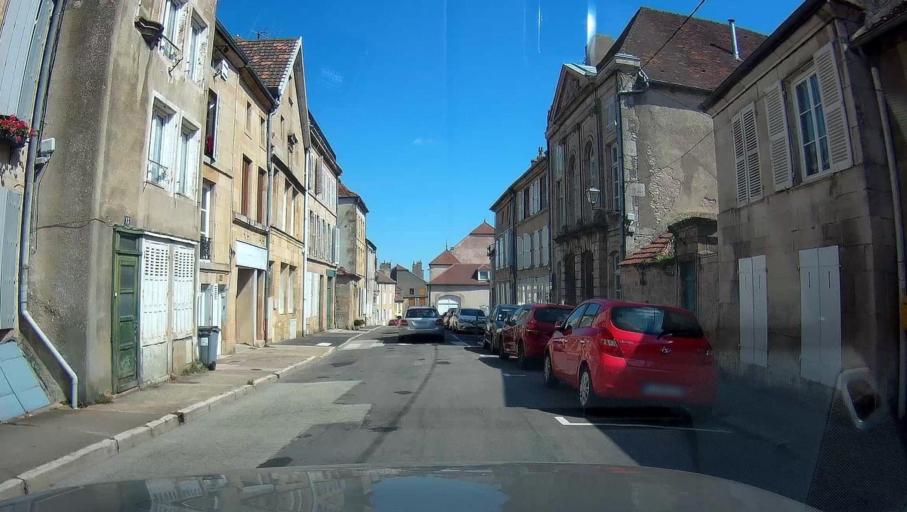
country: FR
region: Champagne-Ardenne
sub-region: Departement de la Haute-Marne
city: Langres
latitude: 47.8660
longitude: 5.3351
